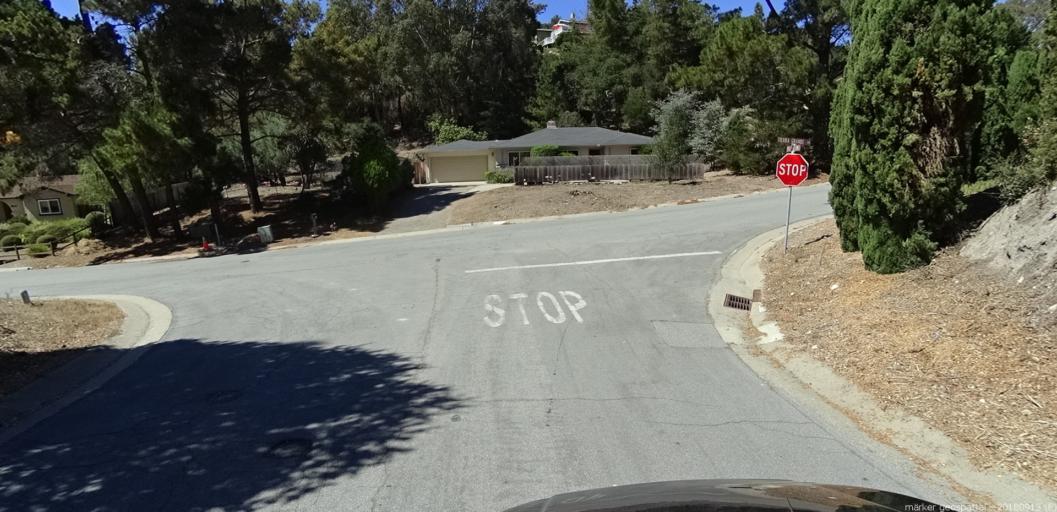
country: US
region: California
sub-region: Monterey County
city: Carmel Valley Village
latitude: 36.5371
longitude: -121.7981
